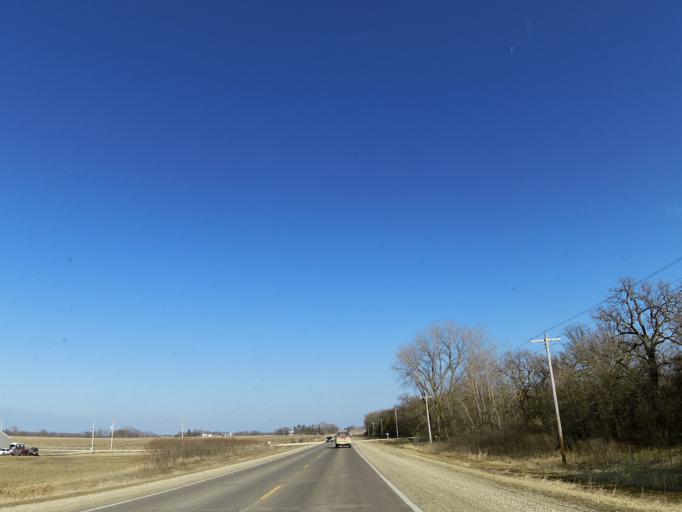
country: US
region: Iowa
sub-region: Worth County
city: Northwood
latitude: 43.4443
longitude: -93.3224
